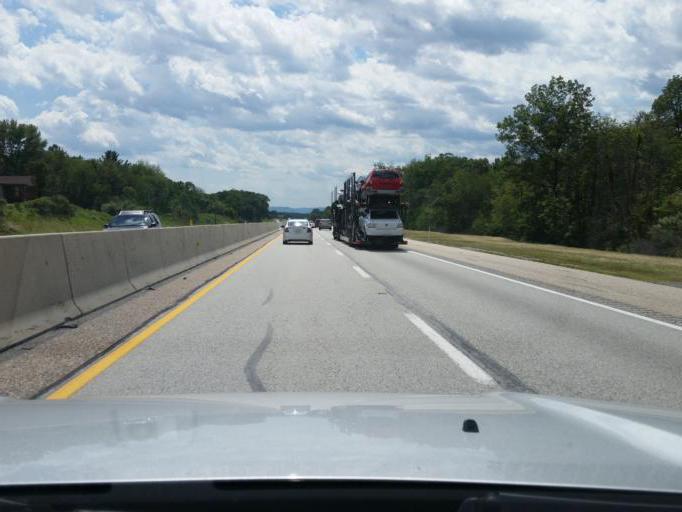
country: US
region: Pennsylvania
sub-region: Franklin County
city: Doylestown
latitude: 40.1475
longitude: -77.7201
